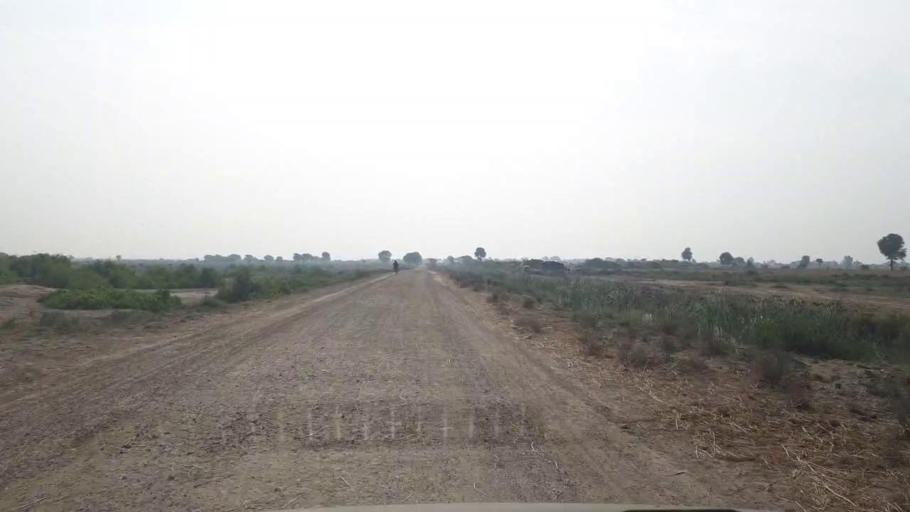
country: PK
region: Sindh
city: Tando Muhammad Khan
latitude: 25.1258
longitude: 68.4979
